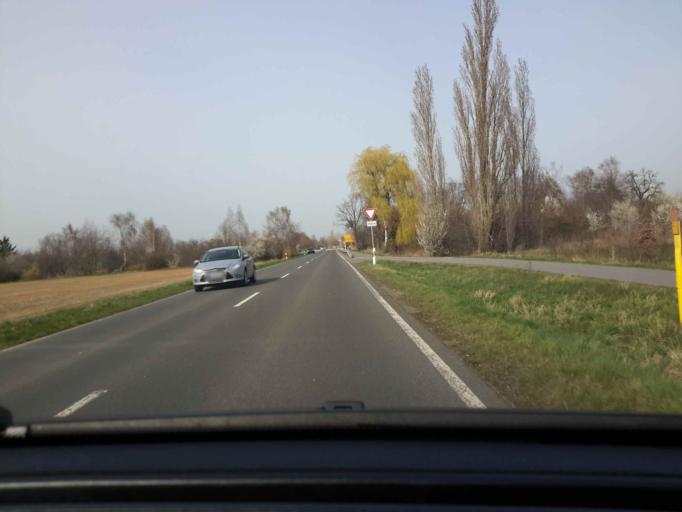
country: DE
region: Saxony
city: Rackwitz
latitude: 51.4312
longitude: 12.3551
